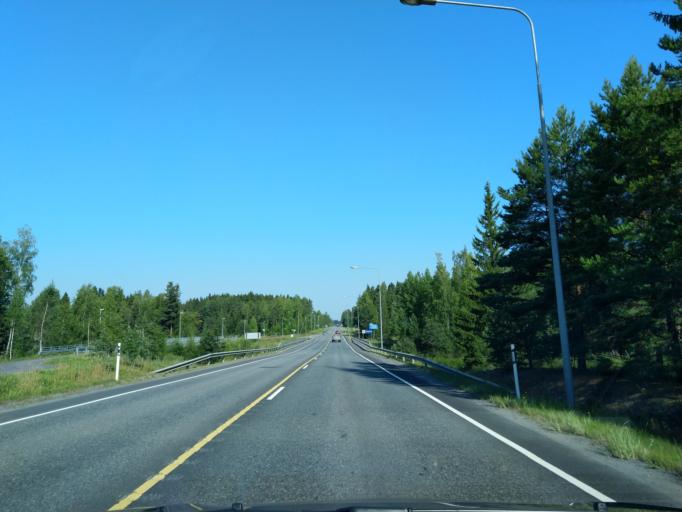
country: FI
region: Haeme
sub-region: Forssa
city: Forssa
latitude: 60.8302
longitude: 23.5635
